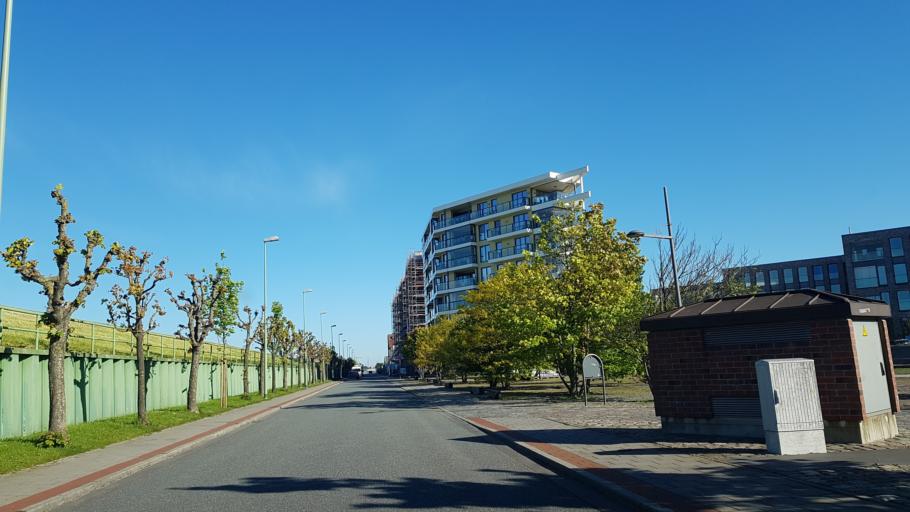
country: DE
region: Bremen
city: Bremerhaven
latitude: 53.5480
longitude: 8.5676
